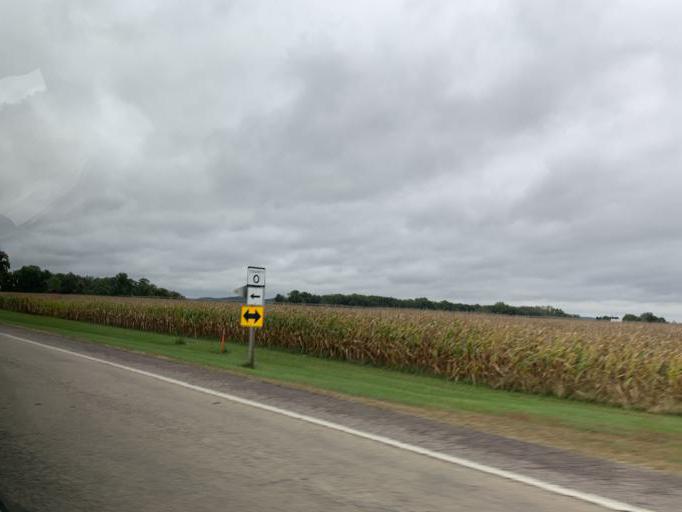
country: US
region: Wisconsin
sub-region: Sauk County
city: Prairie du Sac
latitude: 43.2710
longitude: -89.7892
